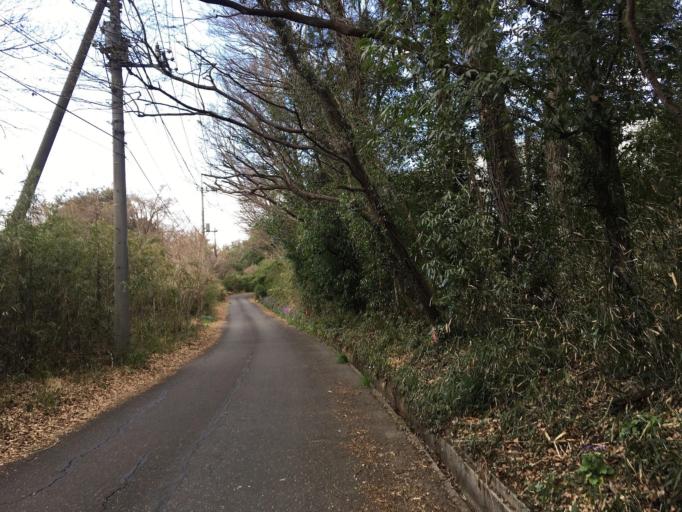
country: JP
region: Saitama
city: Yorii
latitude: 36.1153
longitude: 139.2546
